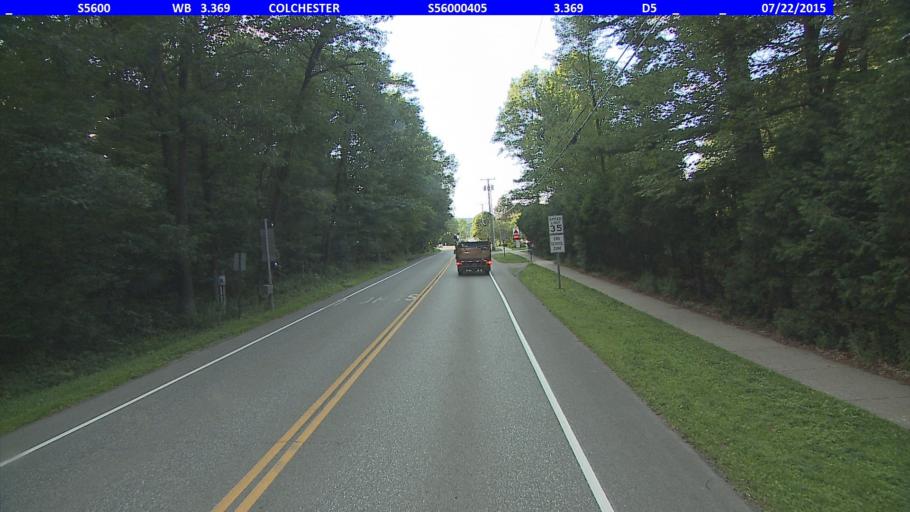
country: US
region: Vermont
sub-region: Chittenden County
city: Winooski
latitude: 44.5427
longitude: -73.2135
